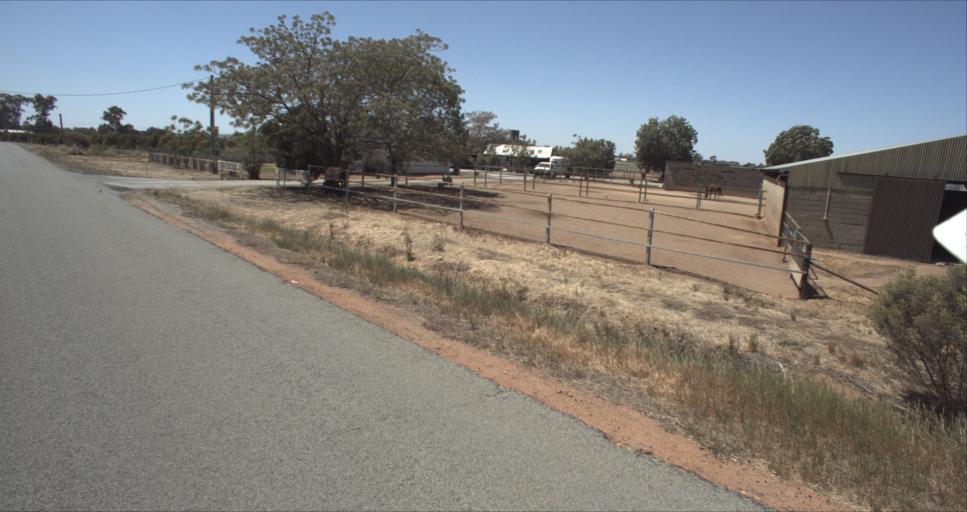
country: AU
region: New South Wales
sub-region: Leeton
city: Leeton
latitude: -34.5354
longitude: 146.3976
